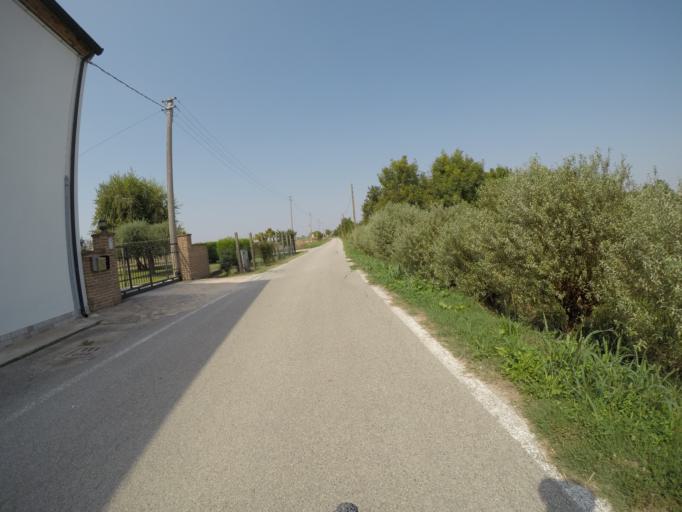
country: IT
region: Veneto
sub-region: Provincia di Rovigo
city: Lendinara
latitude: 45.1098
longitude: 11.5991
